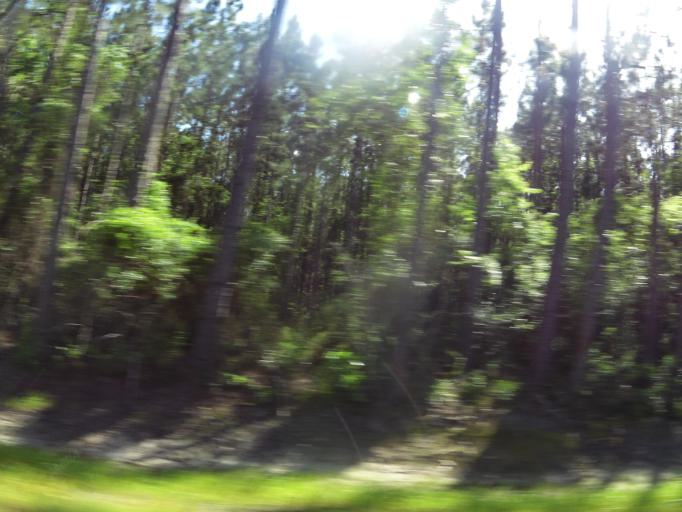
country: US
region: Florida
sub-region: Nassau County
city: Callahan
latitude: 30.6179
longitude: -81.8830
